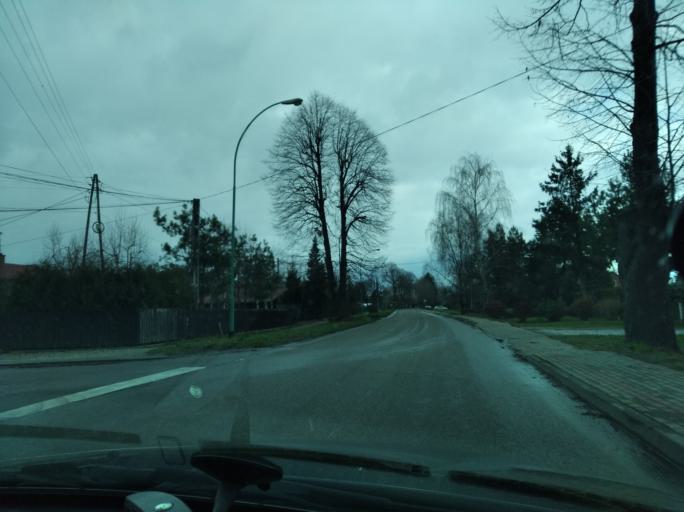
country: PL
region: Subcarpathian Voivodeship
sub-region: Powiat lancucki
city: Lancut
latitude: 50.0904
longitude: 22.2406
